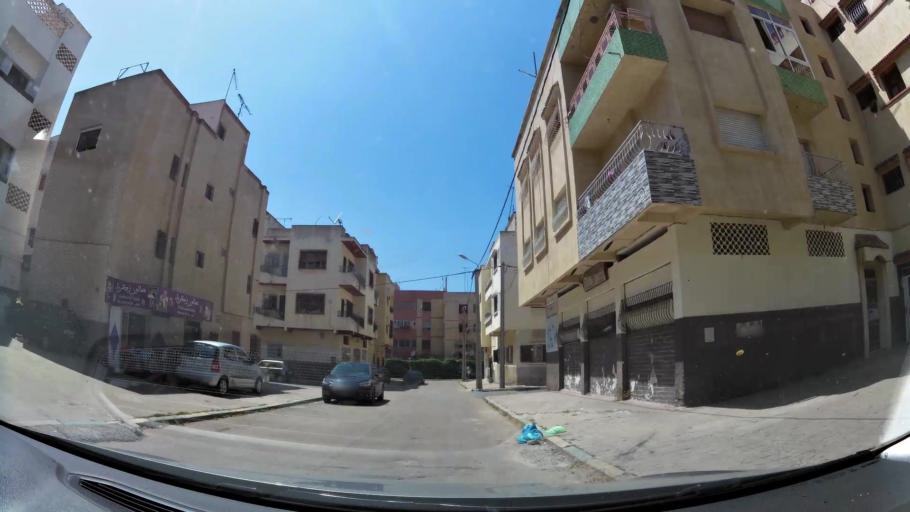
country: MA
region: Rabat-Sale-Zemmour-Zaer
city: Sale
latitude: 34.0435
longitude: -6.7931
